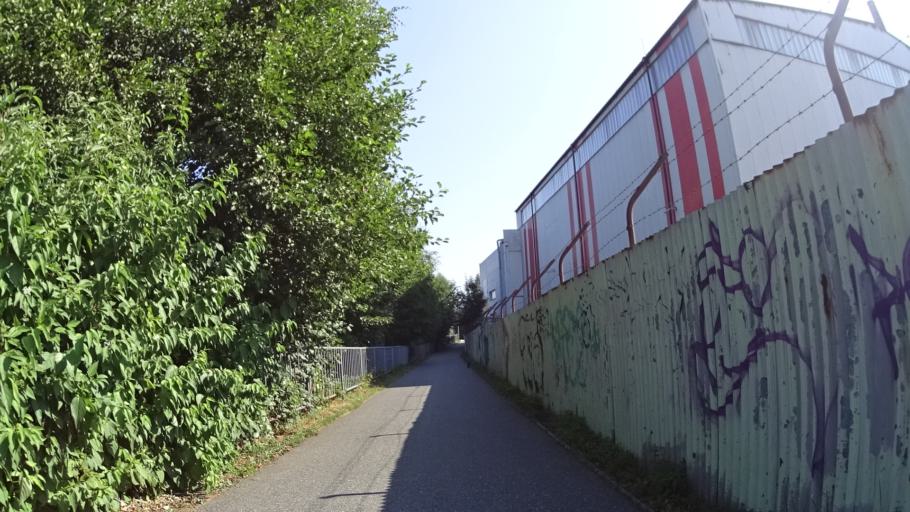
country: CZ
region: Liberecky
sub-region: Okres Liberec
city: Liberec
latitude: 50.7732
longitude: 15.0439
